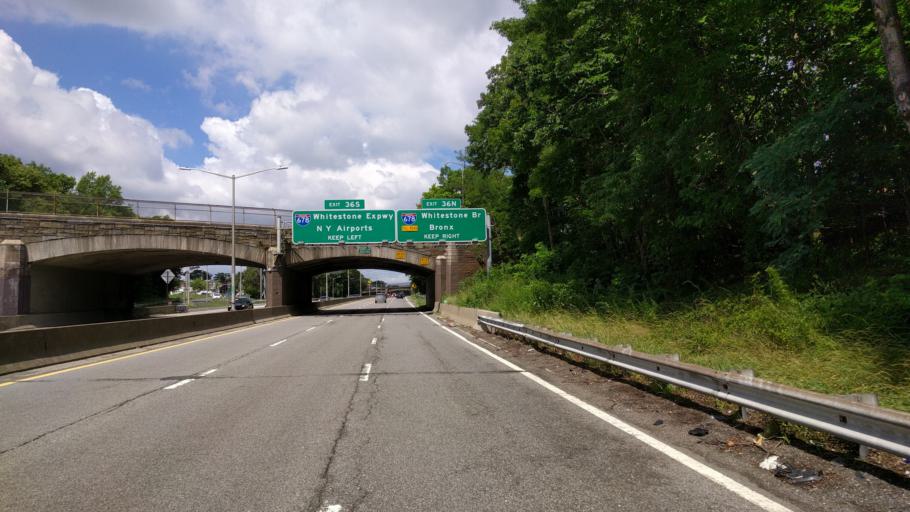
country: US
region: New York
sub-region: Nassau County
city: East Atlantic Beach
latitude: 40.7864
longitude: -73.8054
